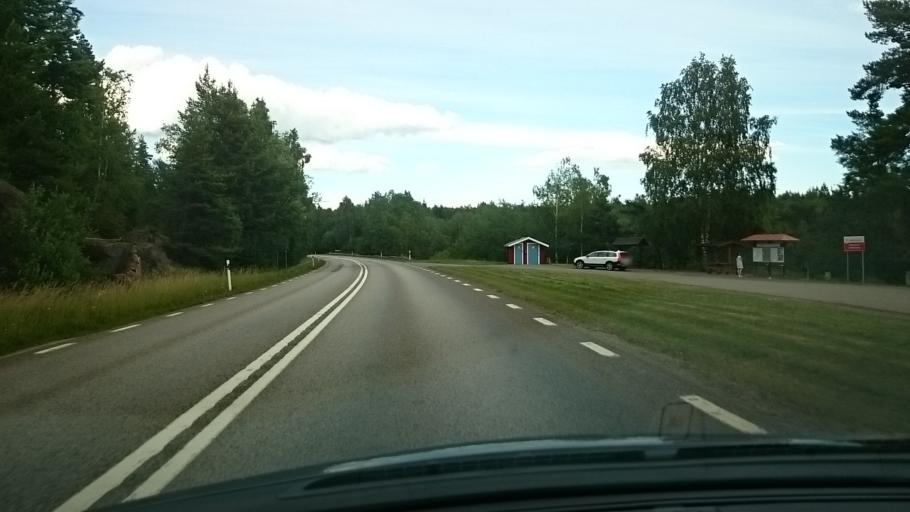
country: SE
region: OErebro
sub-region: Askersunds Kommun
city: Askersund
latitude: 58.7190
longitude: 14.7534
